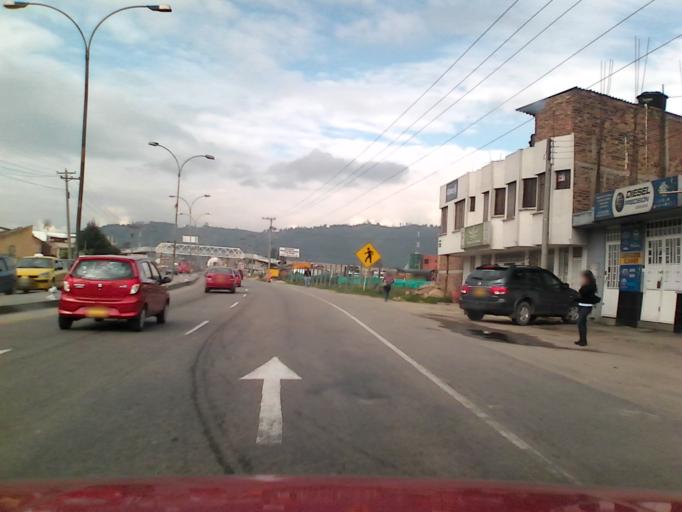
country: CO
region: Boyaca
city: Duitama
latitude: 5.8097
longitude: -73.0162
